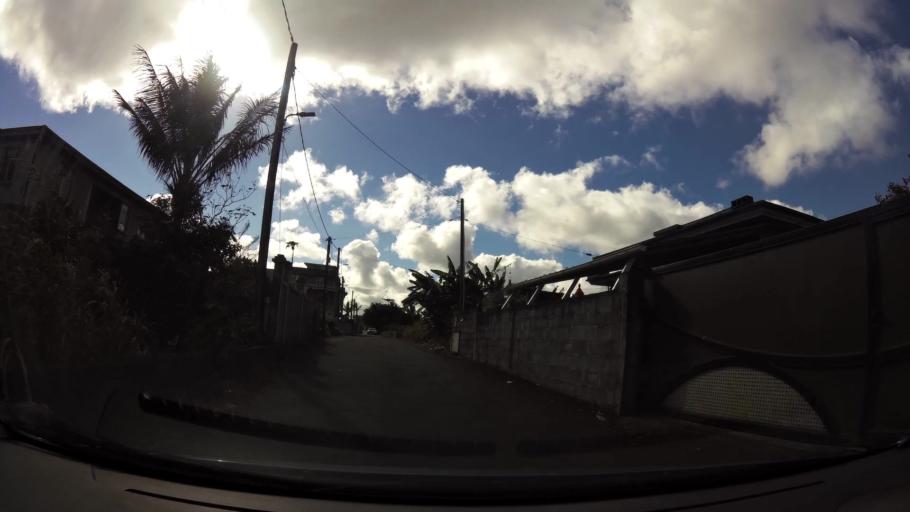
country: MU
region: Plaines Wilhems
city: Curepipe
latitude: -20.2990
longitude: 57.5152
